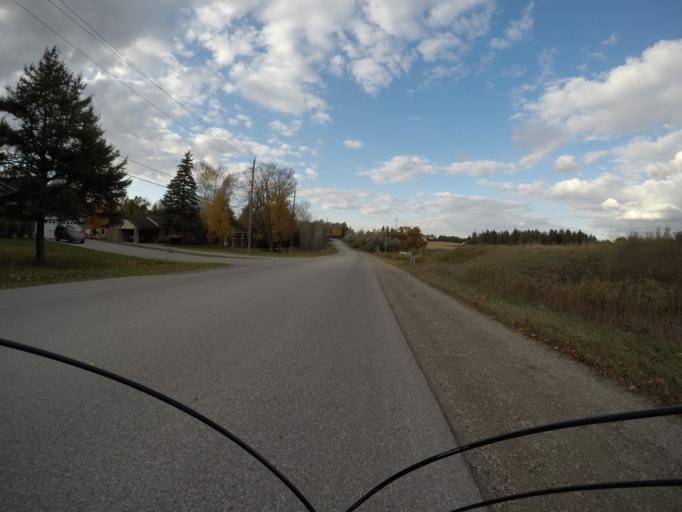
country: CA
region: Ontario
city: Waterloo
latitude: 43.5500
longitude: -80.5532
